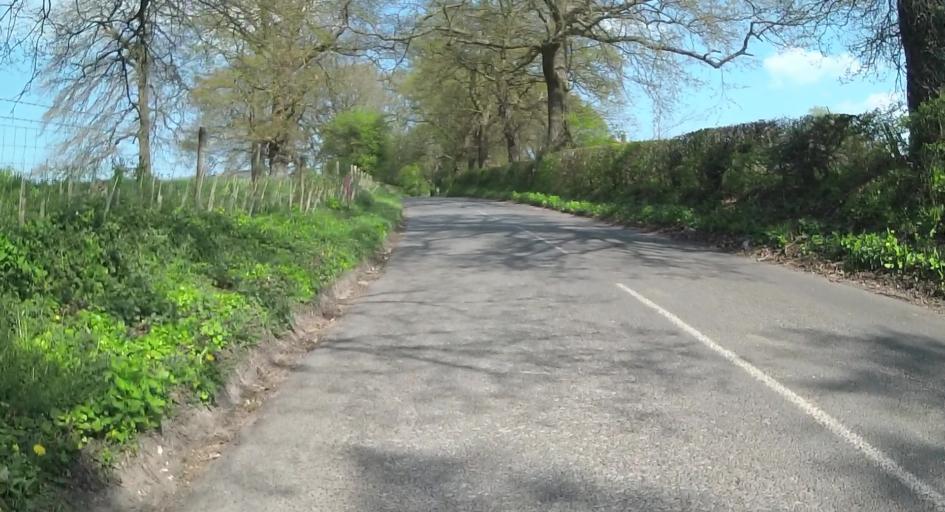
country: GB
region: England
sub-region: Hampshire
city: Basingstoke
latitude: 51.3009
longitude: -1.0924
